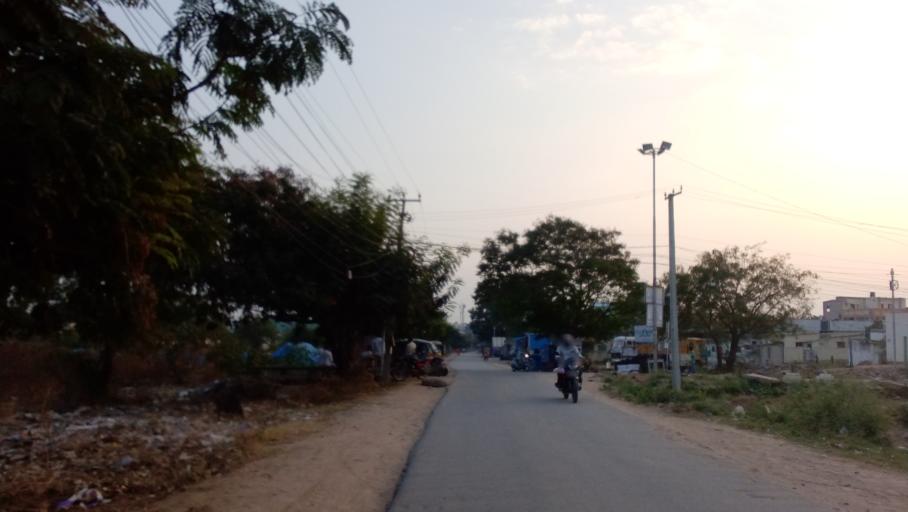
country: IN
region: Telangana
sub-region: Medak
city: Serilingampalle
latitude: 17.5184
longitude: 78.3113
